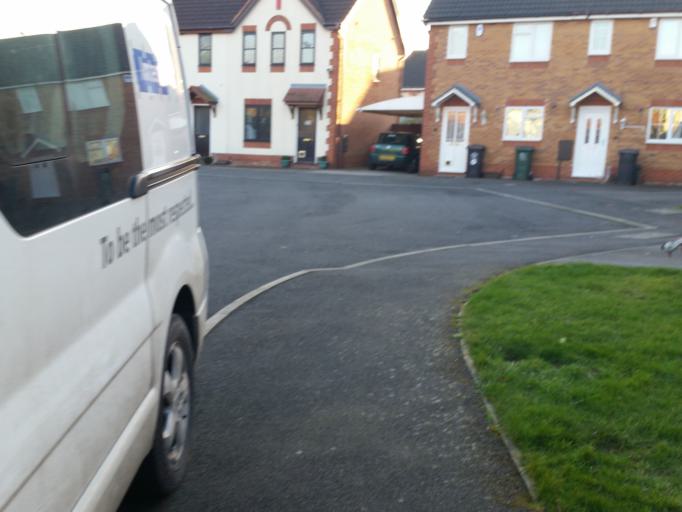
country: GB
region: England
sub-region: Derbyshire
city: Borrowash
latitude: 52.8834
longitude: -1.4109
